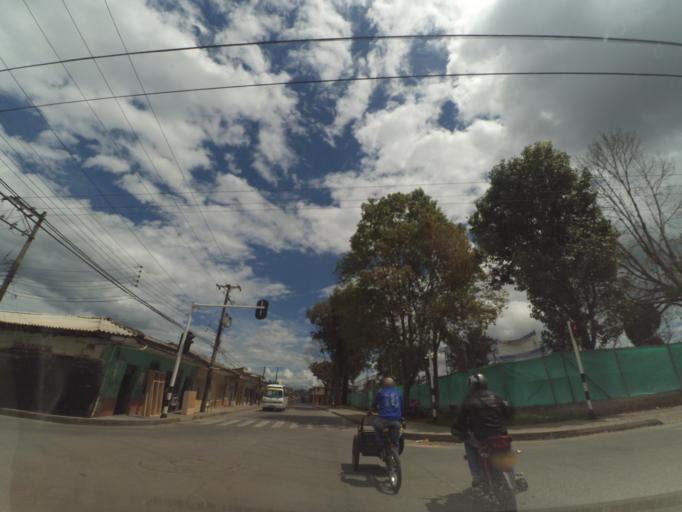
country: CO
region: Cauca
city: Popayan
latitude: 2.4336
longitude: -76.6049
